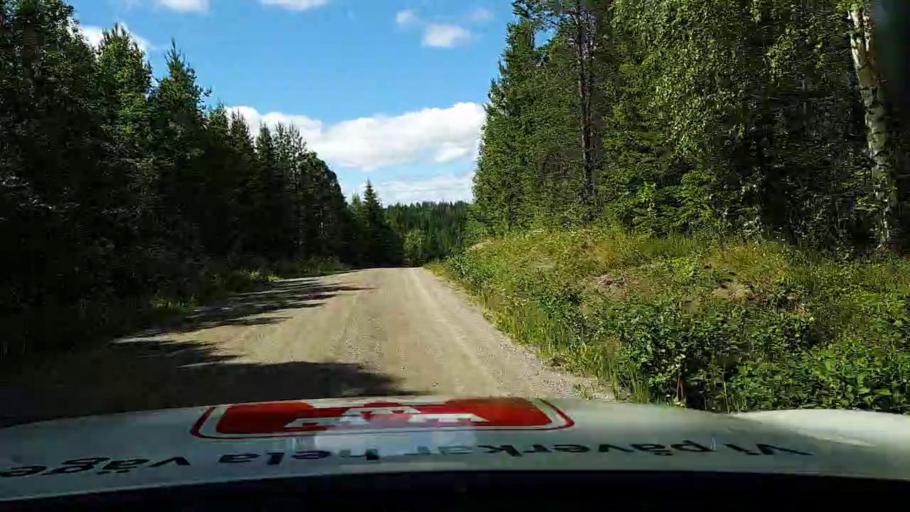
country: SE
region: Jaemtland
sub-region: Braecke Kommun
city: Braecke
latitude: 62.7360
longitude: 15.4854
